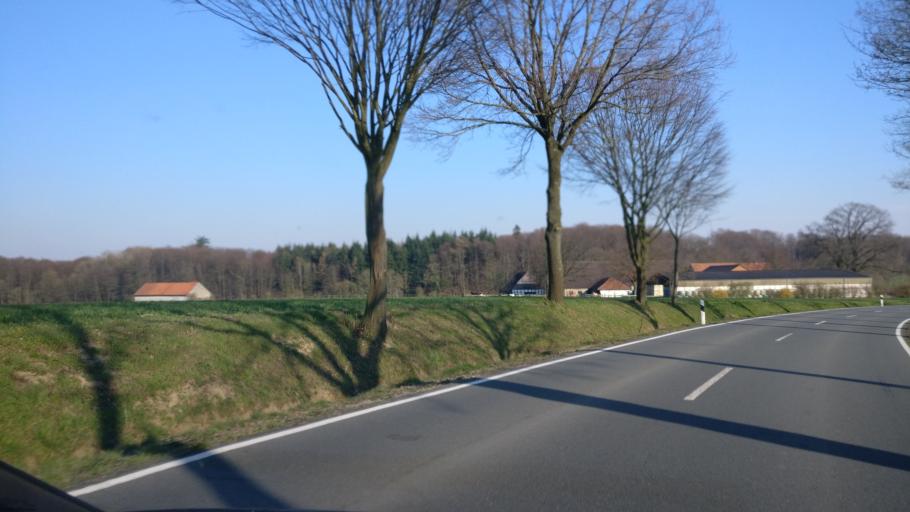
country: DE
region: North Rhine-Westphalia
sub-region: Regierungsbezirk Detmold
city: Lage
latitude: 52.0065
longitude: 8.7501
